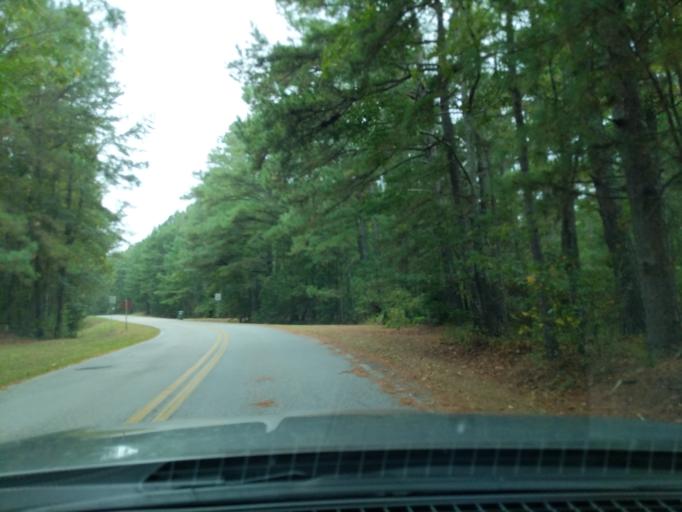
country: US
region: Georgia
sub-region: Columbia County
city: Appling
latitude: 33.6419
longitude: -82.3862
